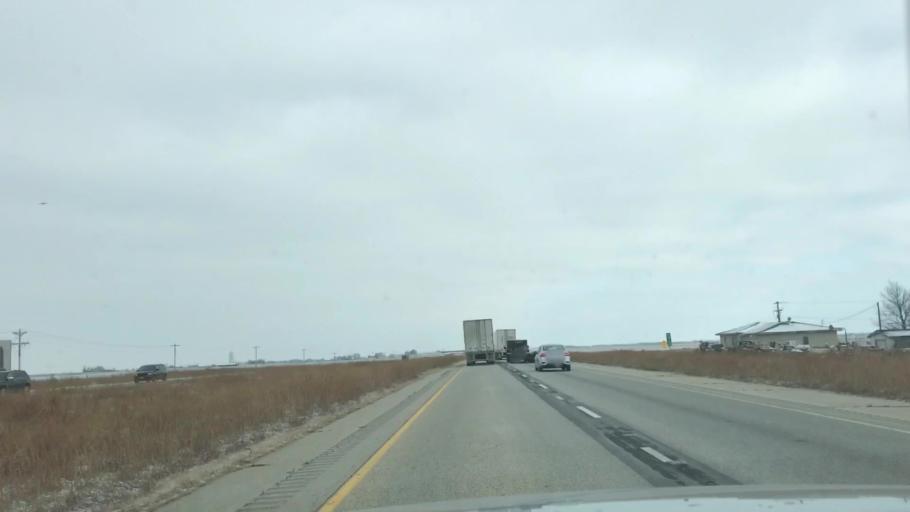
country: US
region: Illinois
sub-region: Sangamon County
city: Divernon
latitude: 39.4641
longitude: -89.6443
